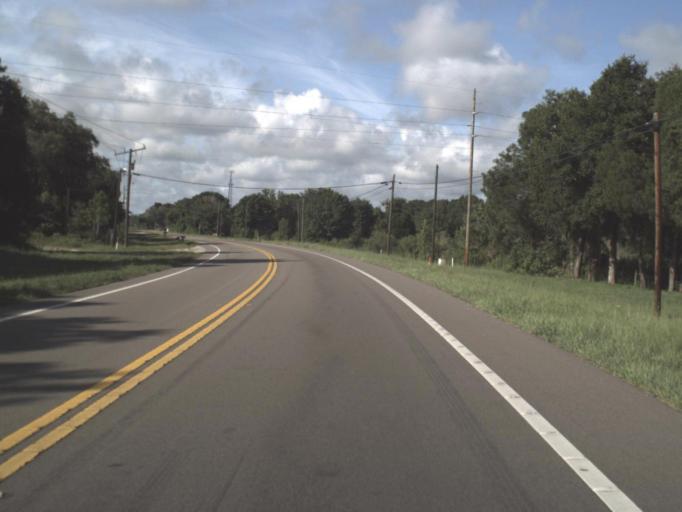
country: US
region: Florida
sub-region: Pasco County
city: Shady Hills
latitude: 28.3619
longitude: -82.5025
